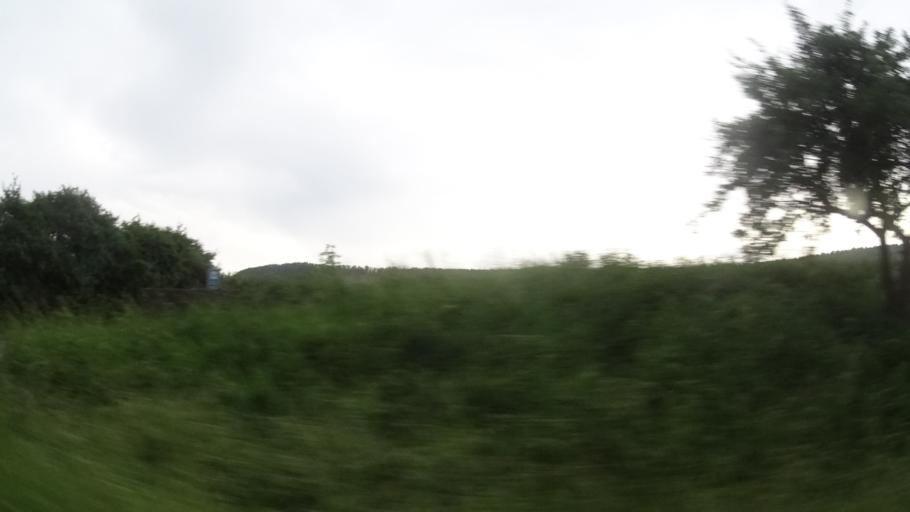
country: DE
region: Lower Saxony
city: Salzhemmendorf
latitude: 52.0476
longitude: 9.5398
